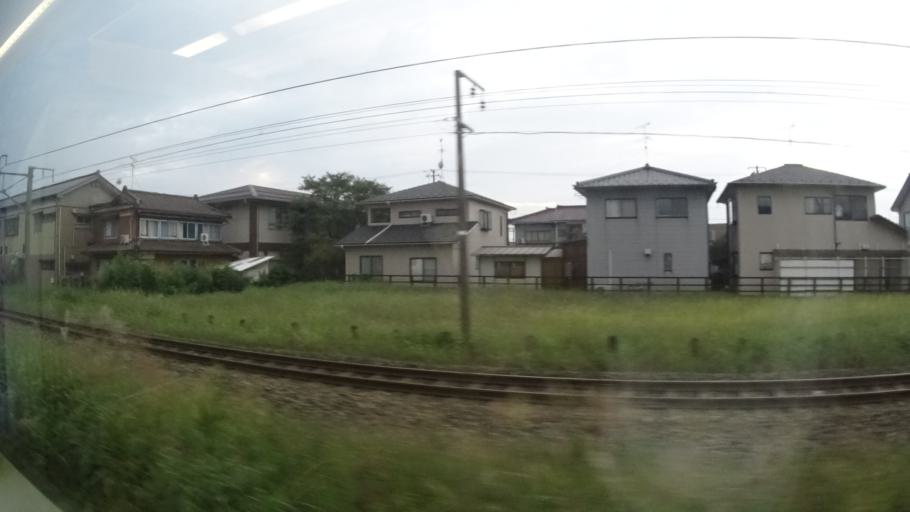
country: JP
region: Niigata
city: Murakami
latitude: 38.1823
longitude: 139.4597
